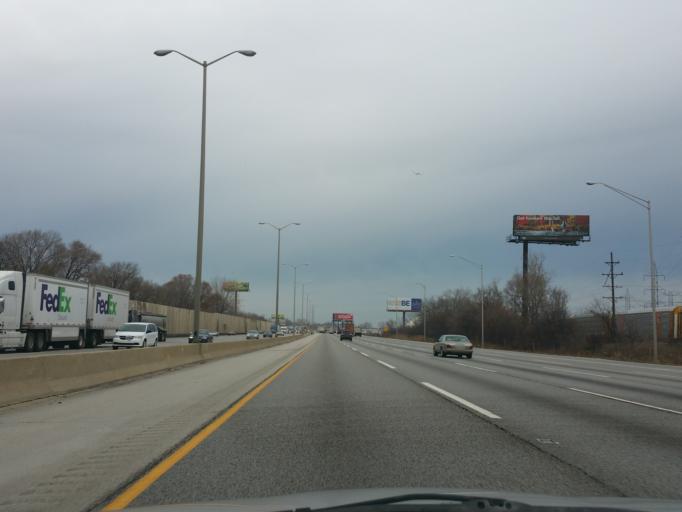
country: US
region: Illinois
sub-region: Cook County
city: Hickory Hills
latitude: 41.7225
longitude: -87.8084
